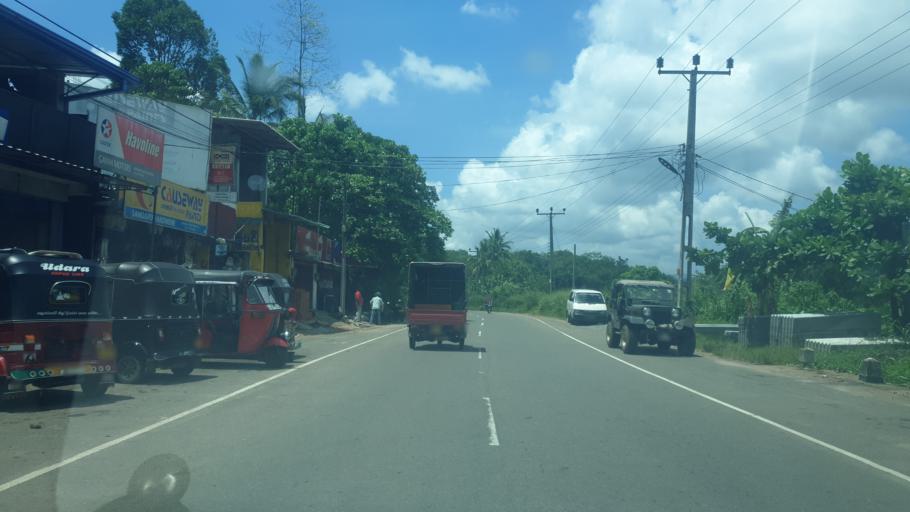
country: LK
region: Western
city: Horawala Junction
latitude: 6.5157
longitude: 80.2351
